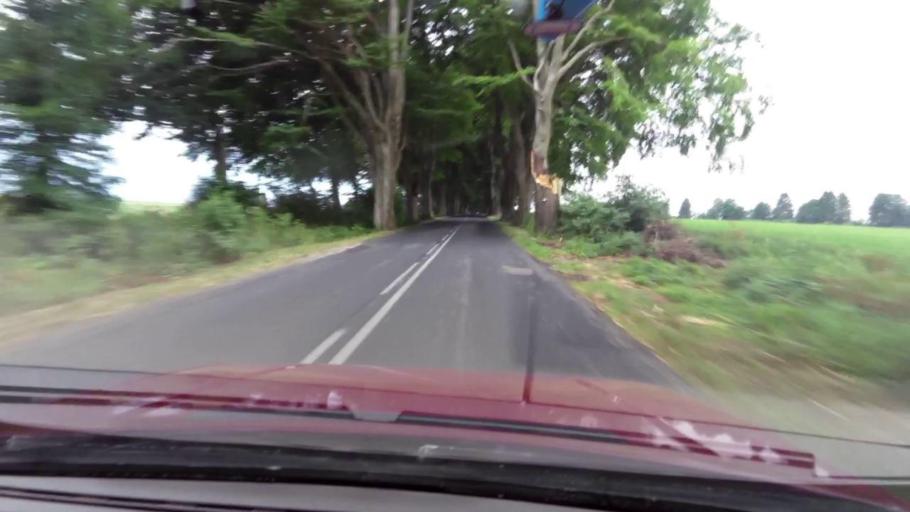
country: PL
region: West Pomeranian Voivodeship
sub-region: Powiat koszalinski
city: Polanow
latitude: 54.1413
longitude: 16.5440
